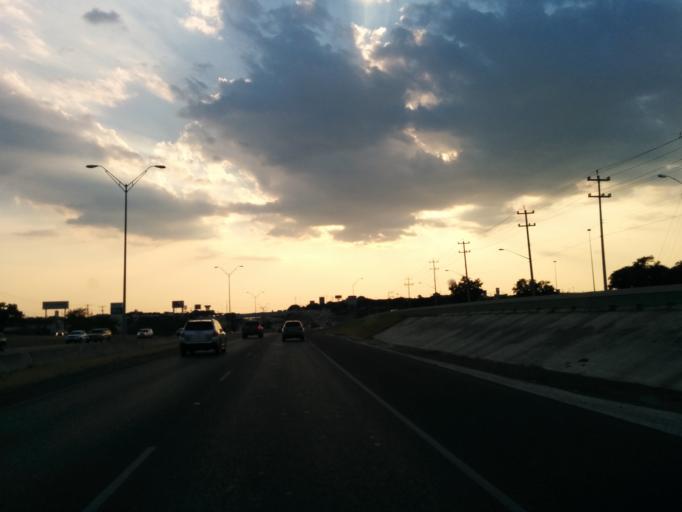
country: US
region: Texas
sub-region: Bexar County
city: Hollywood Park
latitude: 29.6086
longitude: -98.5018
